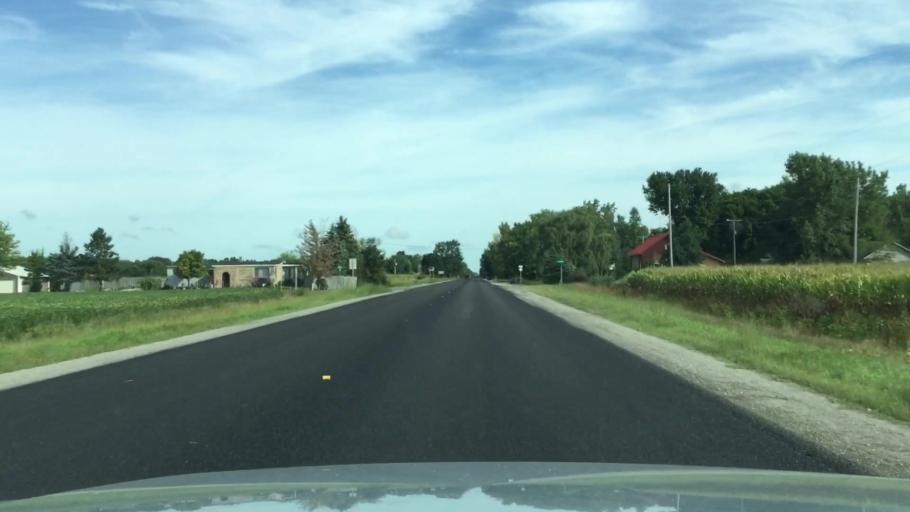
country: US
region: Michigan
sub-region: Genesee County
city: Montrose
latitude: 43.1462
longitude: -83.9295
